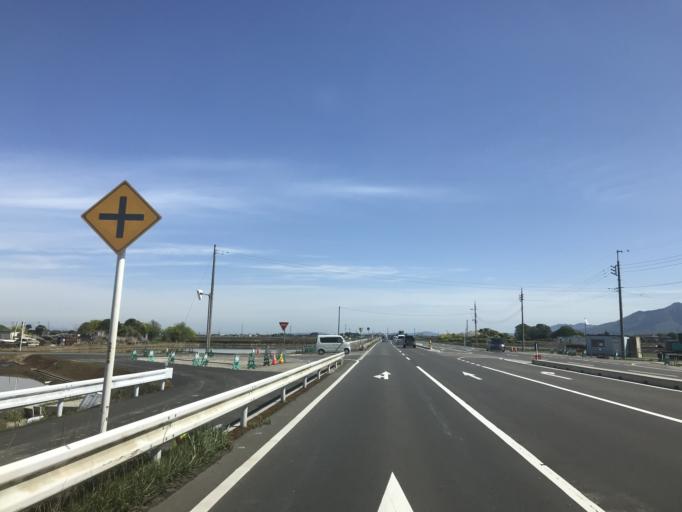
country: JP
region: Ibaraki
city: Ishige
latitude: 36.1403
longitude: 139.9874
